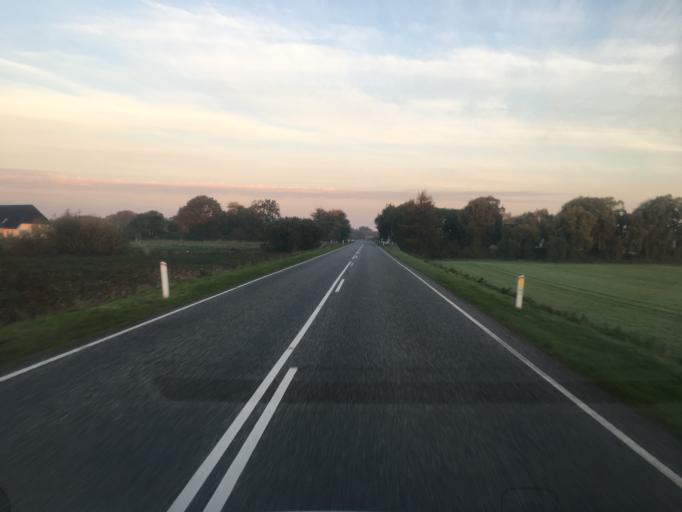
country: DK
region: South Denmark
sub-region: Tonder Kommune
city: Logumkloster
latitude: 55.0318
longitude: 9.0483
